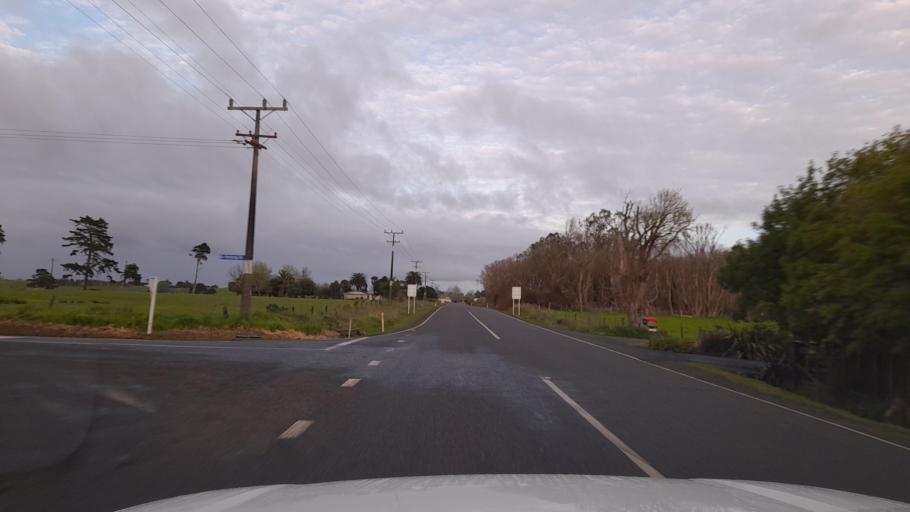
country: NZ
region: Northland
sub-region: Whangarei
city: Maungatapere
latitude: -35.7373
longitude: 174.1362
